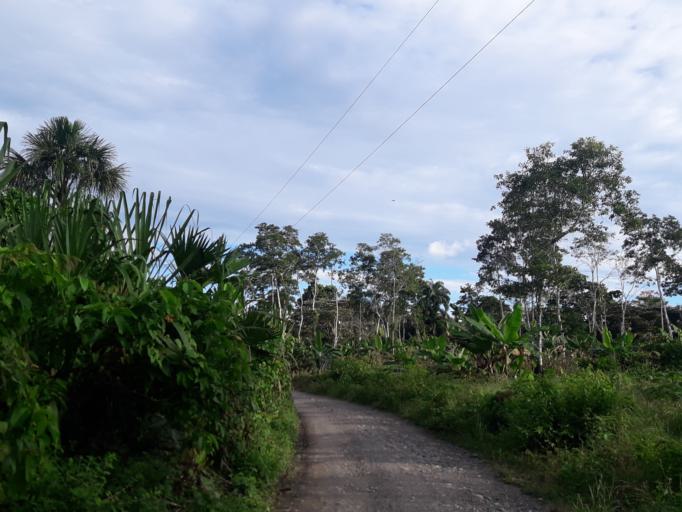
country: EC
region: Orellana
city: Boca Suno
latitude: -0.8971
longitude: -77.3092
